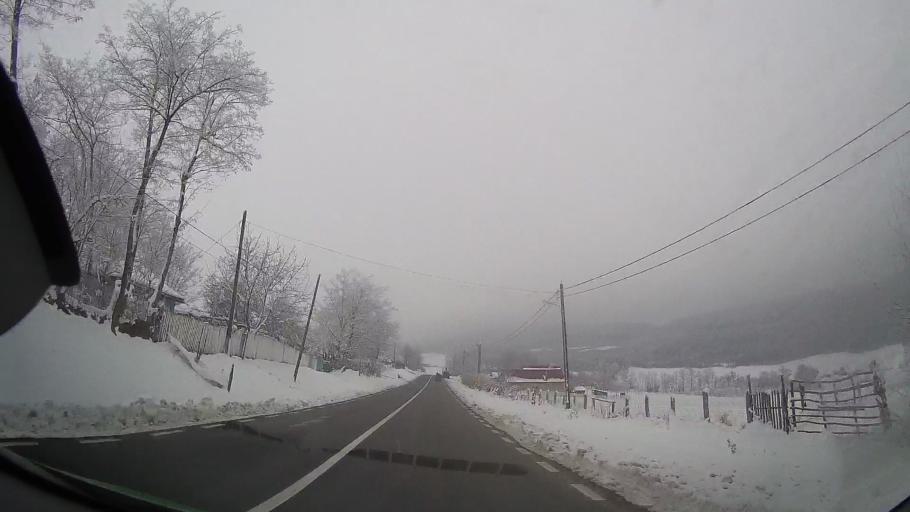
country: RO
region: Neamt
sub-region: Comuna Poenari
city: Poienari
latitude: 46.8777
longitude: 27.1333
